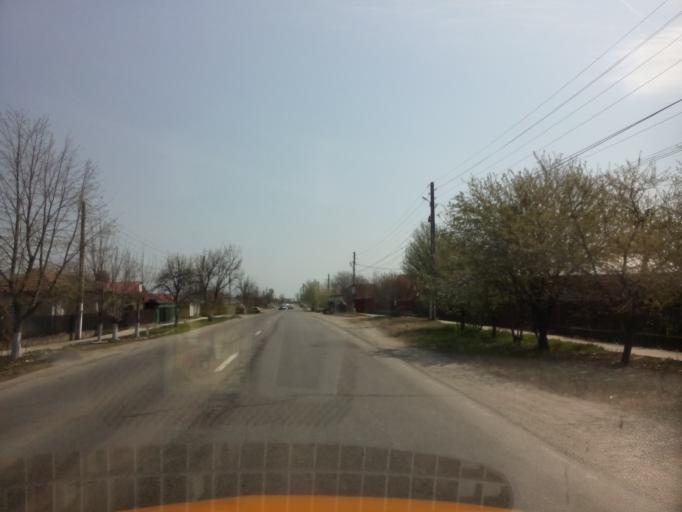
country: RO
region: Calarasi
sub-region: Comuna Soldanu
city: Negoesti
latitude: 44.2315
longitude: 26.4964
